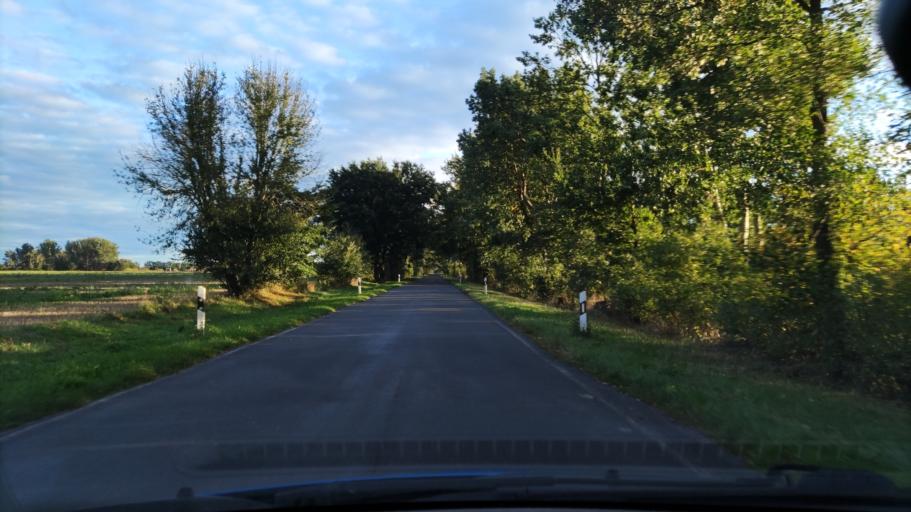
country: DE
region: Lower Saxony
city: Neu Darchau
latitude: 53.3520
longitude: 10.8631
